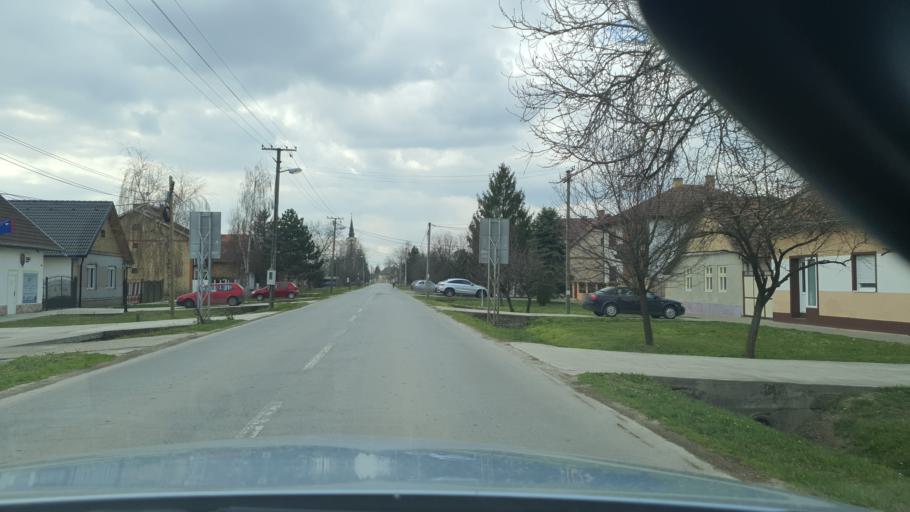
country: RS
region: Autonomna Pokrajina Vojvodina
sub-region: Juznobacki Okrug
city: Bac
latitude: 45.4096
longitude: 19.2985
